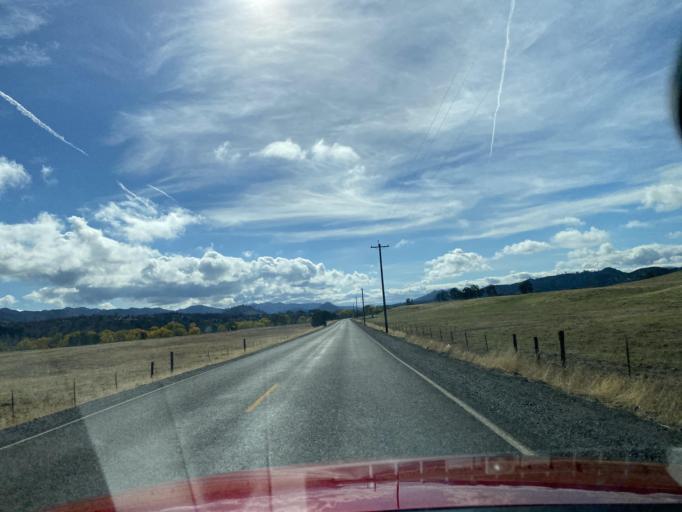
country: US
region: California
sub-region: Glenn County
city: Willows
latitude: 39.4686
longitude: -122.5123
